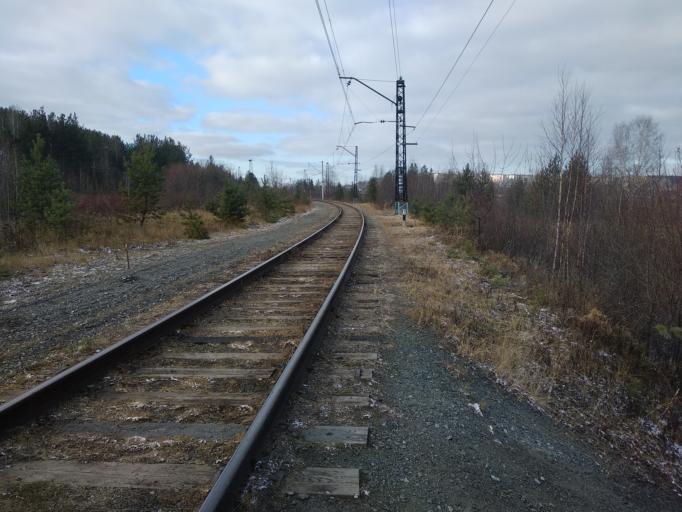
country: RU
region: Sverdlovsk
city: Karpinsk
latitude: 59.7548
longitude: 60.0370
